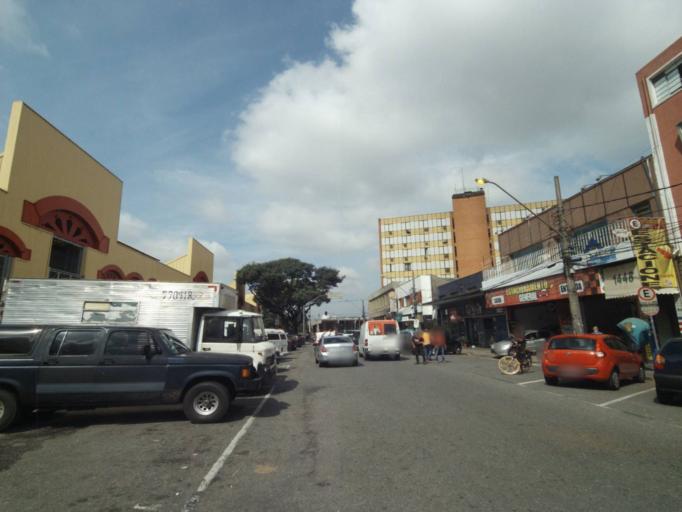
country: BR
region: Parana
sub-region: Curitiba
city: Curitiba
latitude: -25.4347
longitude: -49.2574
